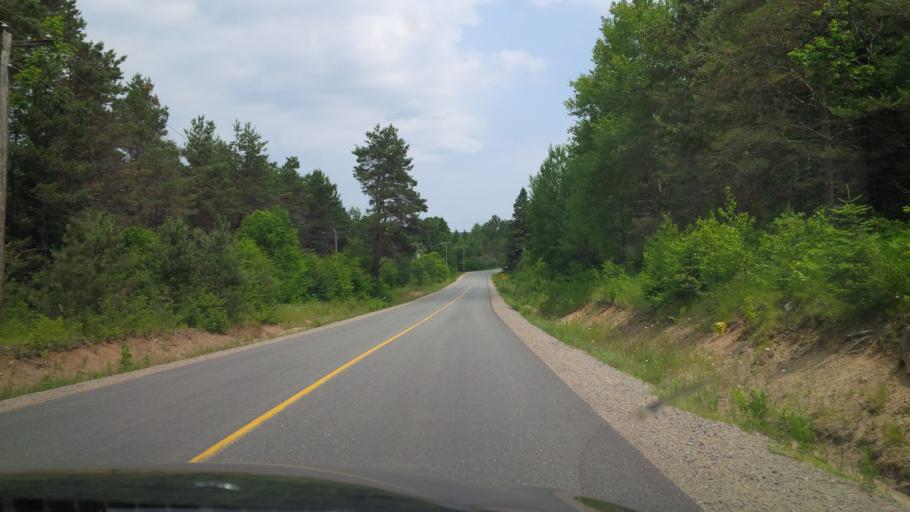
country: CA
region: Ontario
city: Huntsville
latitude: 45.6125
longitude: -79.1704
